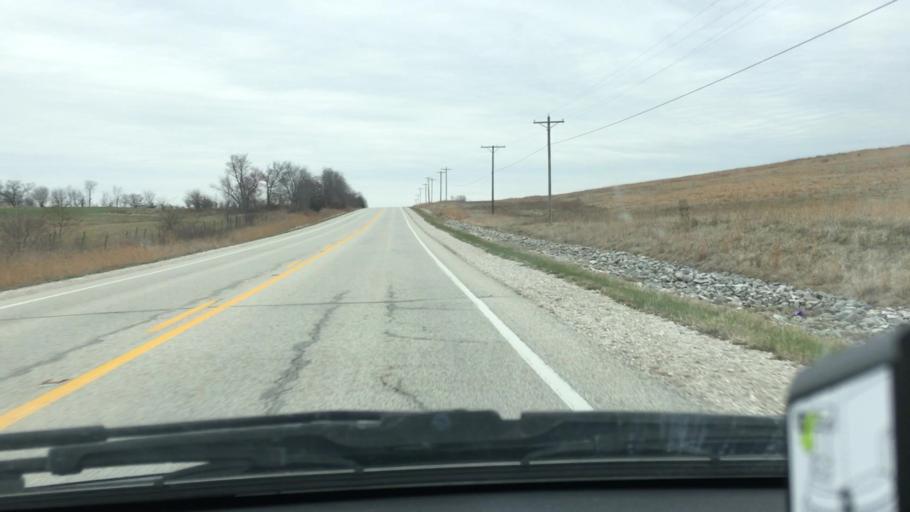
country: US
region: Indiana
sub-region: Greene County
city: Bloomfield
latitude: 39.0112
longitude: -87.0162
